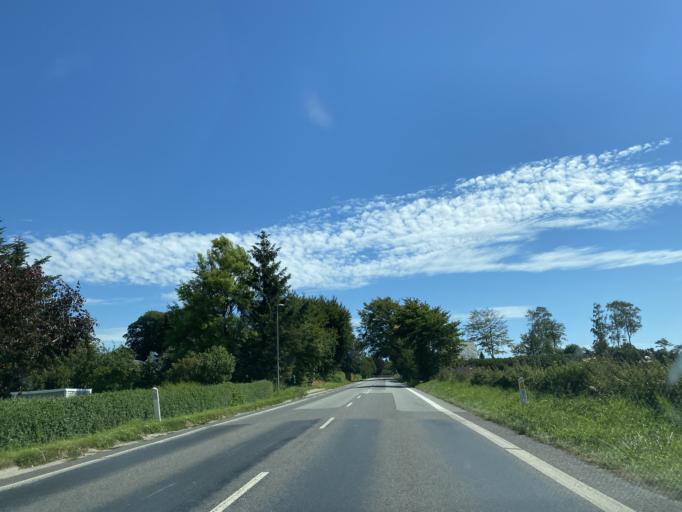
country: DK
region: South Denmark
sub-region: Odense Kommune
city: Bellinge
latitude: 55.2090
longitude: 10.3402
